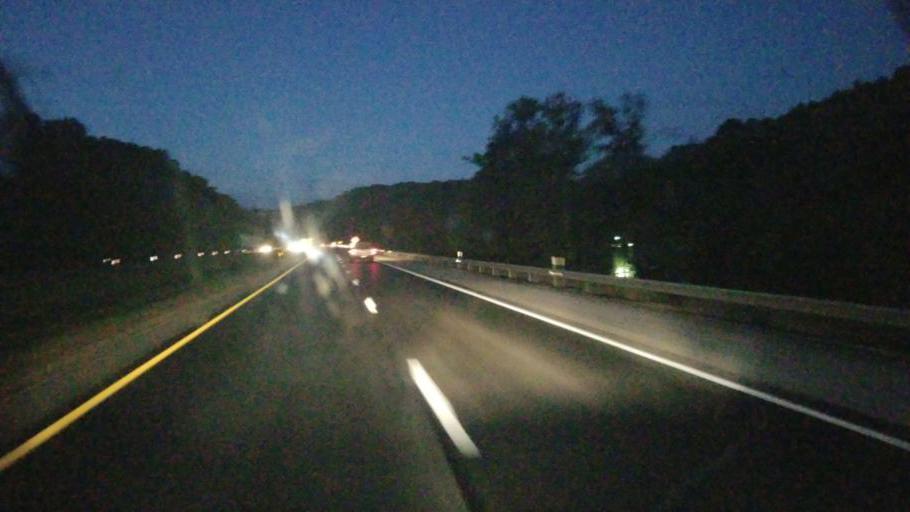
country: US
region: West Virginia
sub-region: Monongalia County
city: Star City
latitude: 39.7660
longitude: -80.0811
